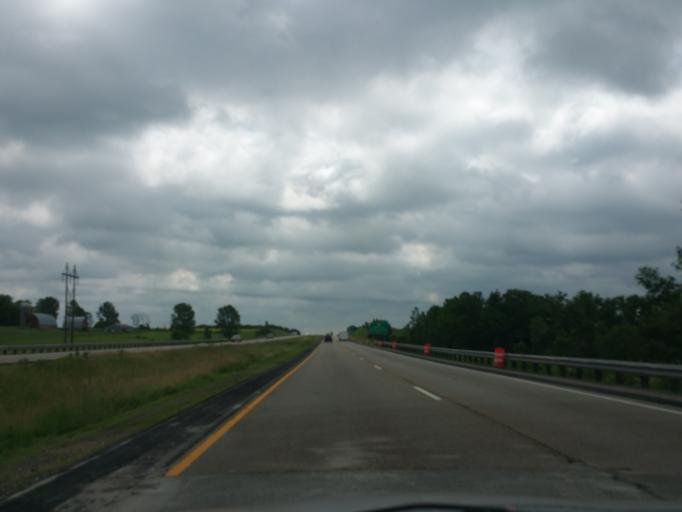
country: US
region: Wisconsin
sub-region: Saint Croix County
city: Woodville
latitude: 44.9353
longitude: -92.3059
